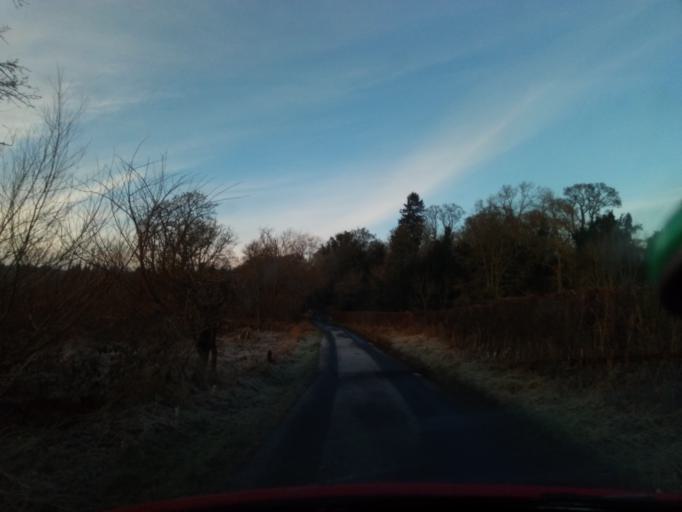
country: GB
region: Scotland
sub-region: The Scottish Borders
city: Hawick
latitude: 55.4546
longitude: -2.7171
